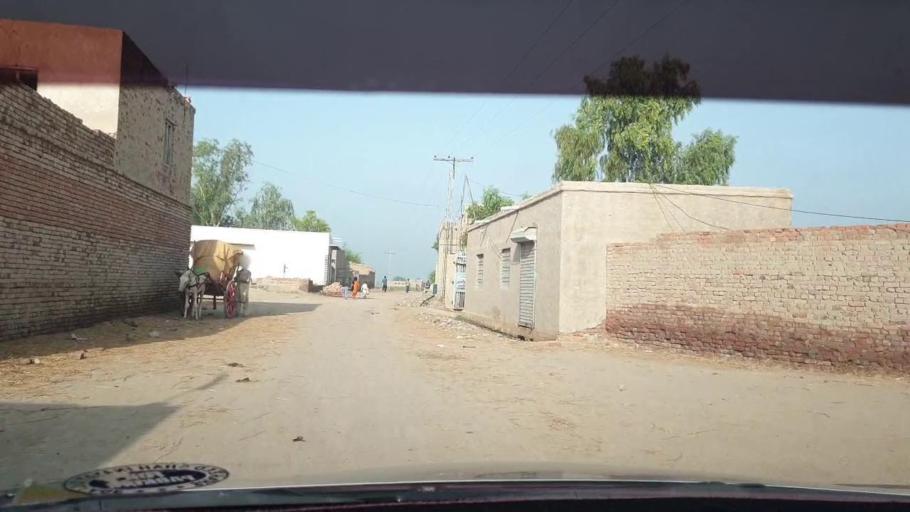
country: PK
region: Sindh
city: Goth Garelo
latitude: 27.4839
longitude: 68.0344
